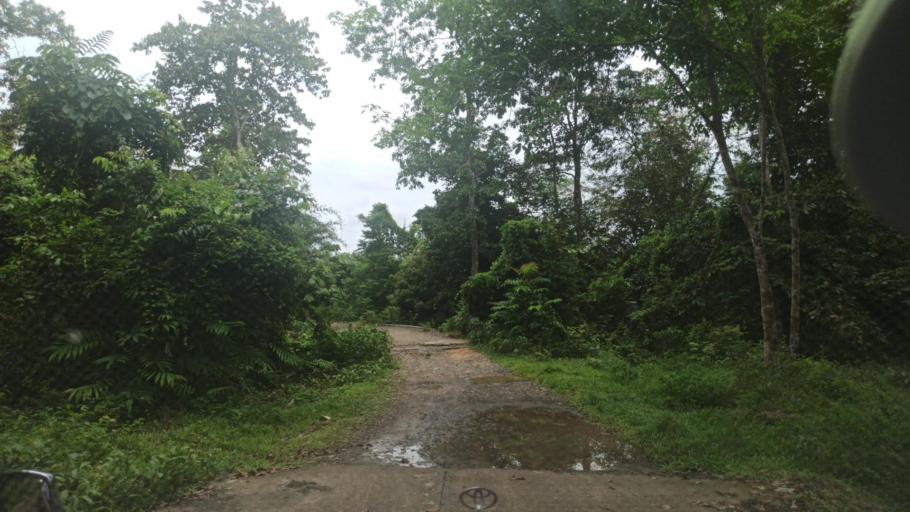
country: ID
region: South Sumatra
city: Gunungmenang
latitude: -3.2460
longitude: 103.8450
